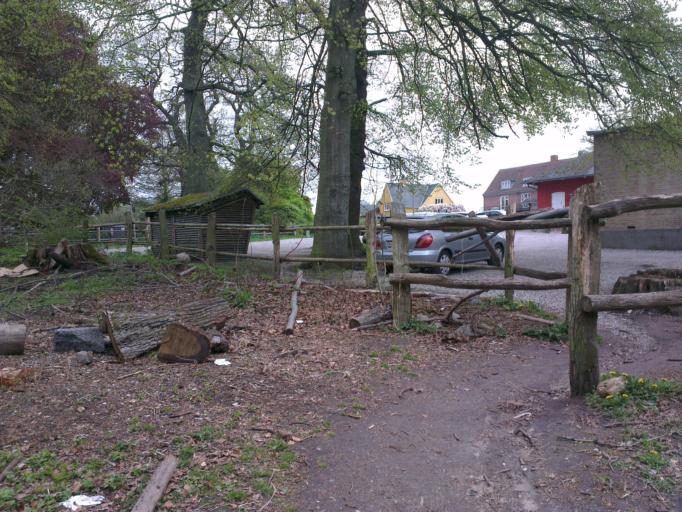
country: DK
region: Capital Region
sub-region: Frederikssund Kommune
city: Jaegerspris
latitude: 55.8558
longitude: 11.9822
